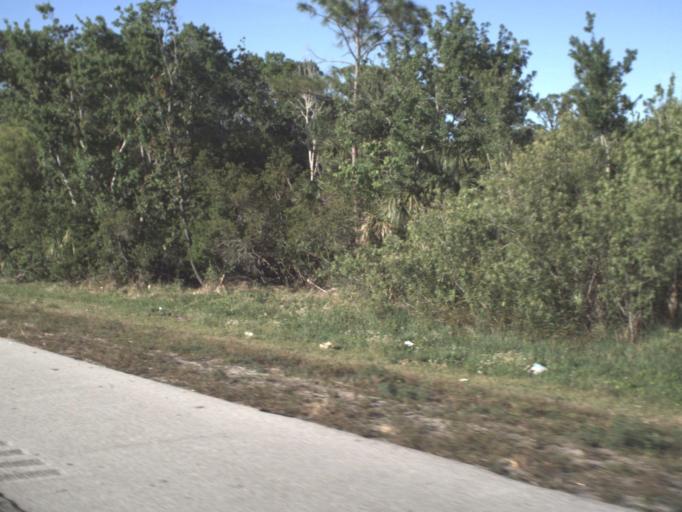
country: US
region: Florida
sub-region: Brevard County
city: South Patrick Shores
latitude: 28.1728
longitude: -80.7057
